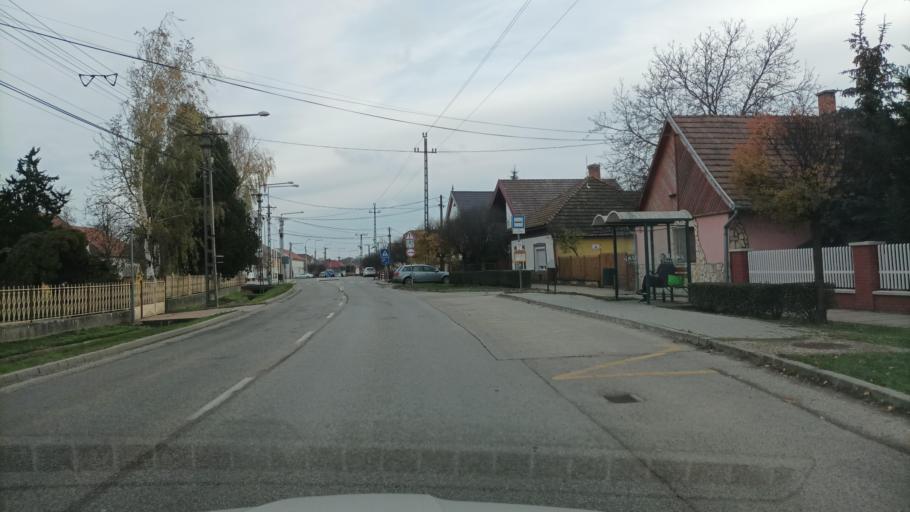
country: HU
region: Pest
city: Ocsa
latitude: 47.2935
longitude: 19.2259
